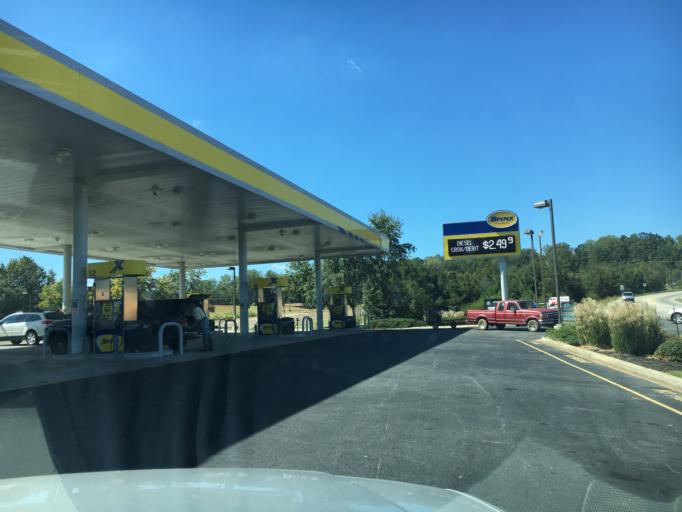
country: US
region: South Carolina
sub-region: Pickens County
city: Liberty
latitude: 34.7758
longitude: -82.6722
